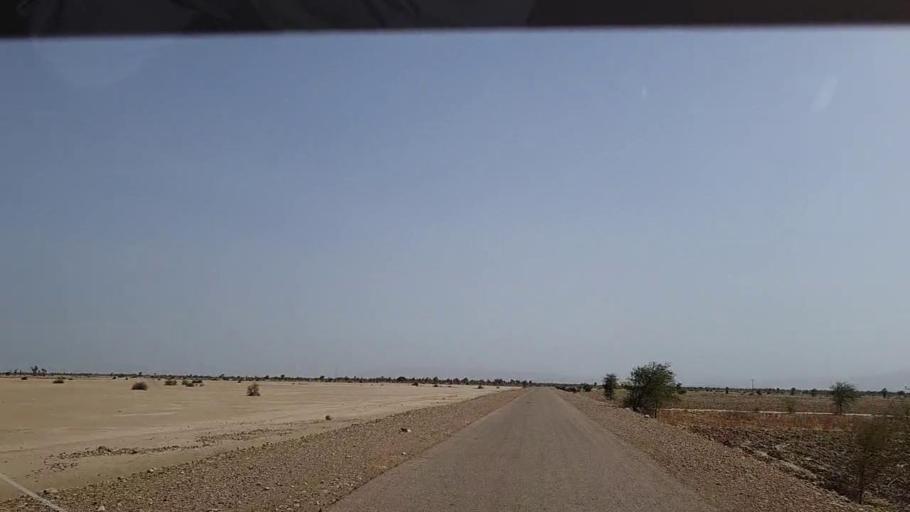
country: PK
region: Sindh
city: Johi
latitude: 26.6667
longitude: 67.5086
